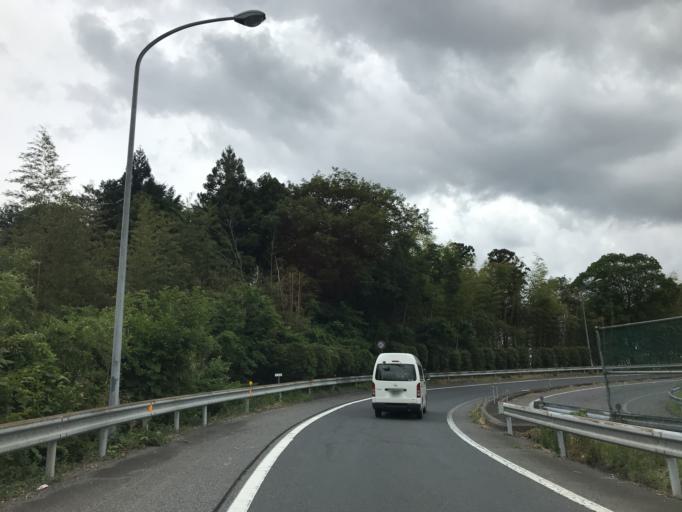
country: JP
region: Ibaraki
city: Ishioka
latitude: 36.1704
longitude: 140.2523
